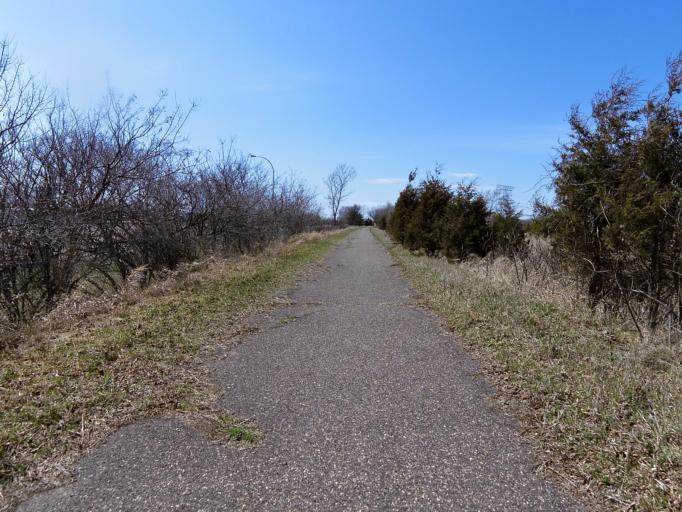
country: US
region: Minnesota
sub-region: Washington County
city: Lakeland
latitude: 44.9512
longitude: -92.8111
